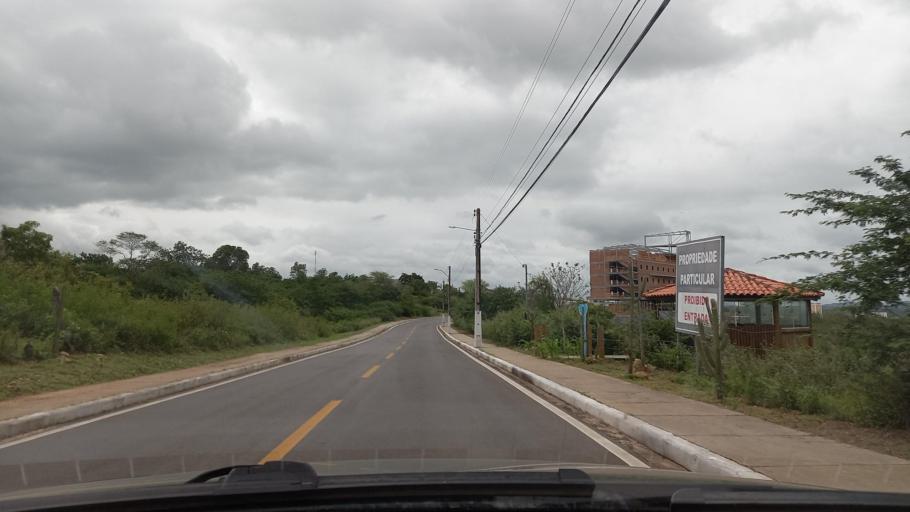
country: BR
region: Sergipe
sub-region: Caninde De Sao Francisco
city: Caninde de Sao Francisco
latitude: -9.6168
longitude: -37.7651
